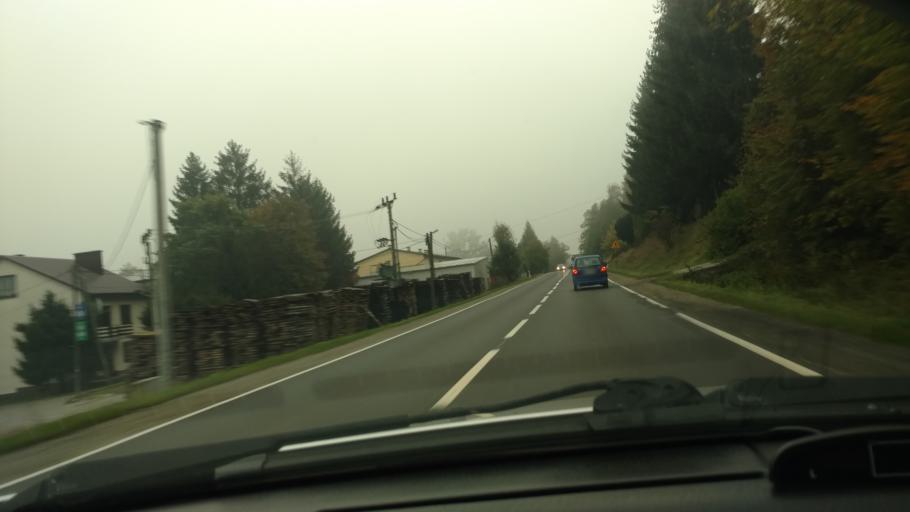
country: PL
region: Subcarpathian Voivodeship
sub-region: Powiat strzyzowski
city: Frysztak
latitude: 49.8363
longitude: 21.6118
